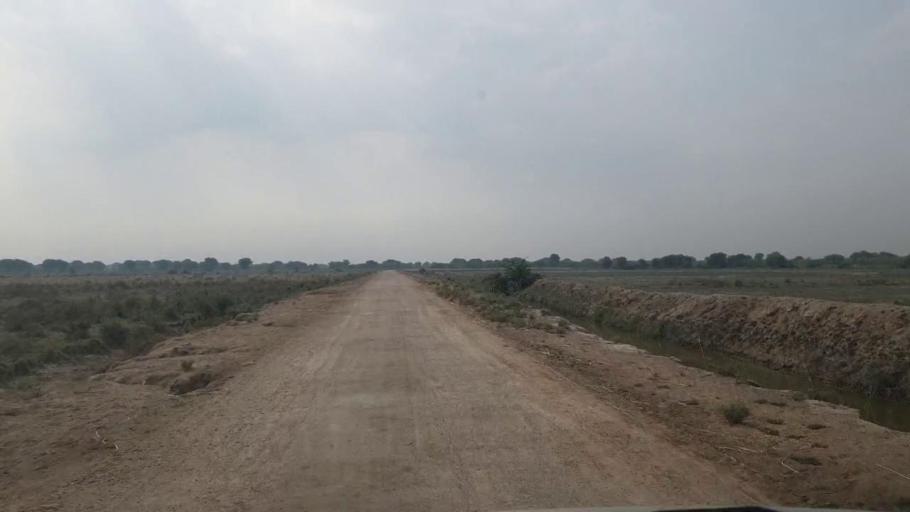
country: PK
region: Sindh
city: Talhar
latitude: 24.8653
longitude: 68.8352
